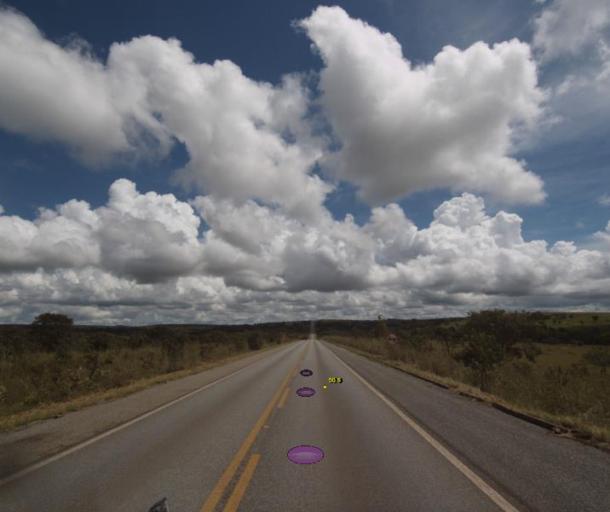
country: BR
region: Goias
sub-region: Pirenopolis
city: Pirenopolis
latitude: -15.7507
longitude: -48.6223
